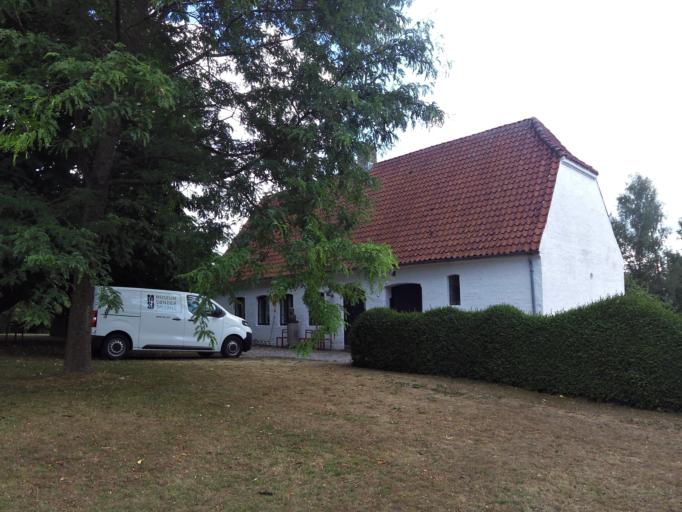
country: DK
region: South Denmark
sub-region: Aabenraa Kommune
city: Aabenraa
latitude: 55.0386
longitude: 9.4139
